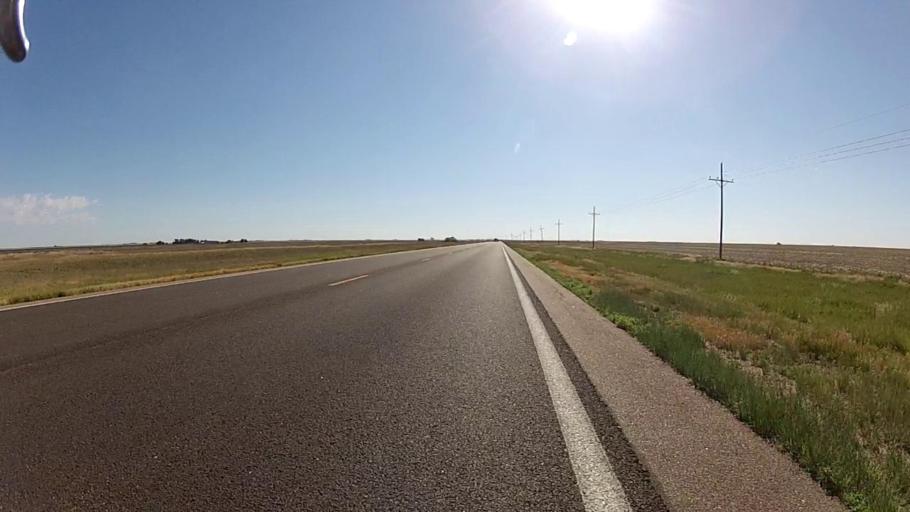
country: US
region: Kansas
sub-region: Haskell County
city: Sublette
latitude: 37.5543
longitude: -100.5878
